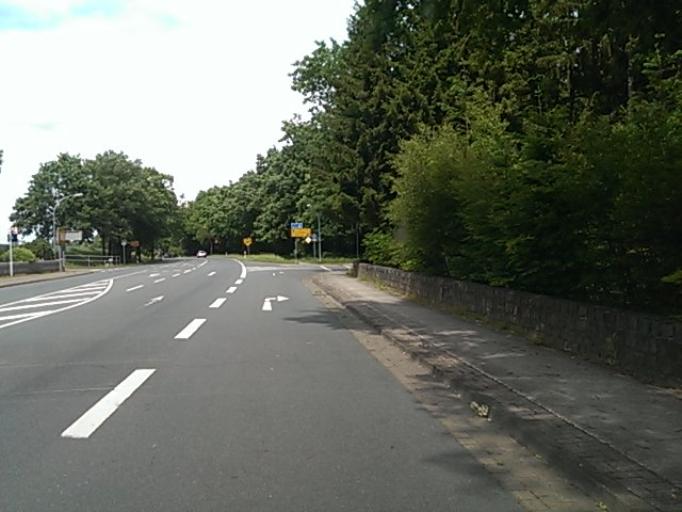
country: DE
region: Lower Saxony
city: Bergen
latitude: 52.7721
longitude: 9.9791
